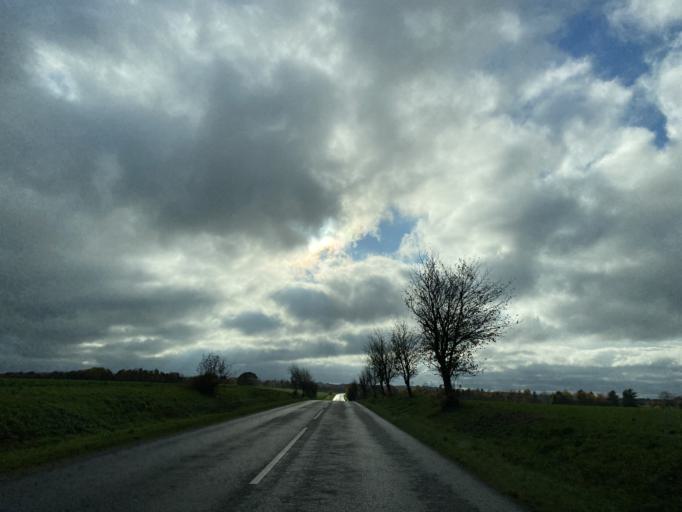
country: DK
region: Central Jutland
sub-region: Favrskov Kommune
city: Hammel
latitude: 56.2410
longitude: 9.7547
